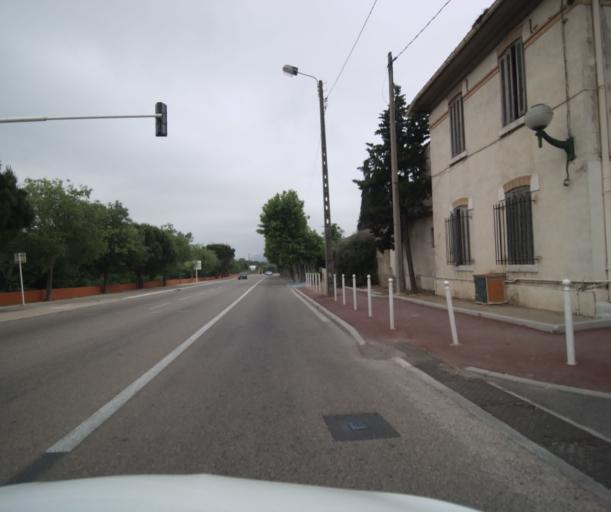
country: FR
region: Provence-Alpes-Cote d'Azur
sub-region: Departement du Var
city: La Seyne-sur-Mer
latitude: 43.1237
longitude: 5.8958
